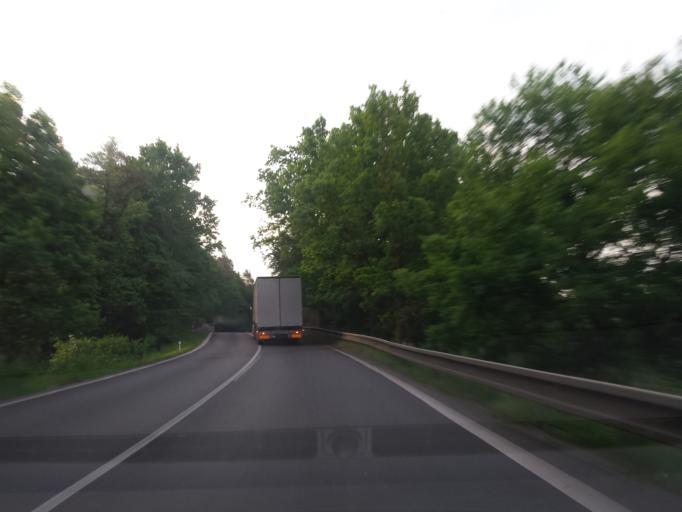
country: CZ
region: Liberecky
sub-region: Okres Ceska Lipa
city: Ceska Lipa
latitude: 50.6228
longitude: 14.5357
